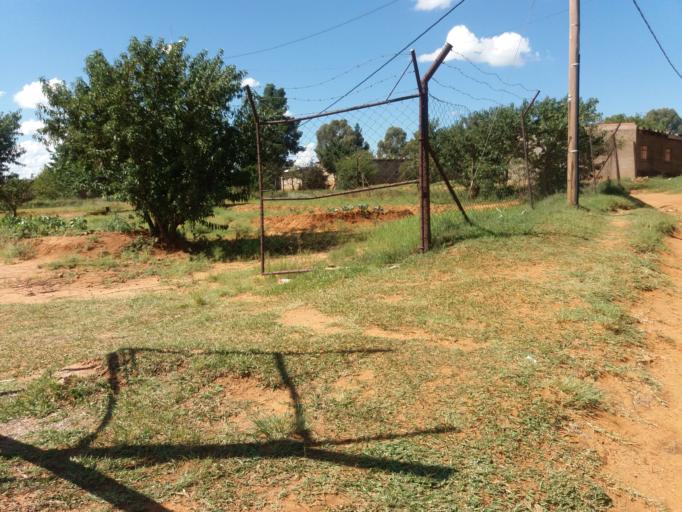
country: LS
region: Maseru
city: Maseru
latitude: -29.3705
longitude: 27.5056
